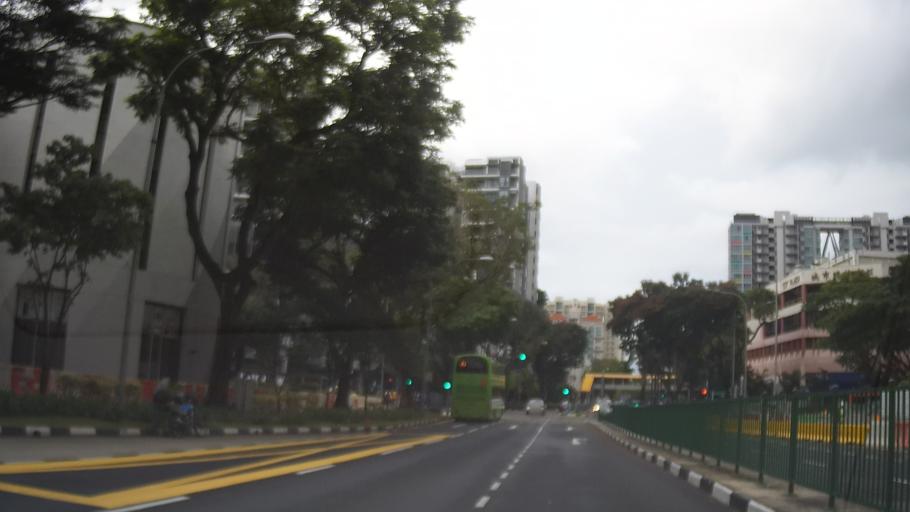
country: SG
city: Singapore
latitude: 1.3162
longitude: 103.8940
